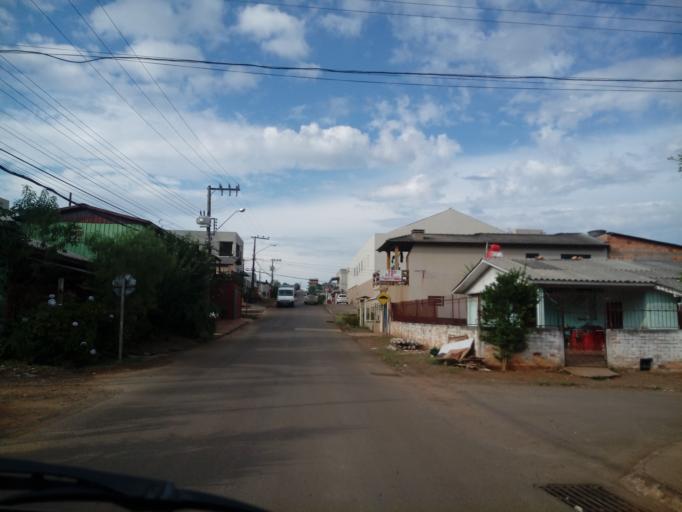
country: BR
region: Santa Catarina
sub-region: Chapeco
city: Chapeco
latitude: -27.0942
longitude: -52.5914
